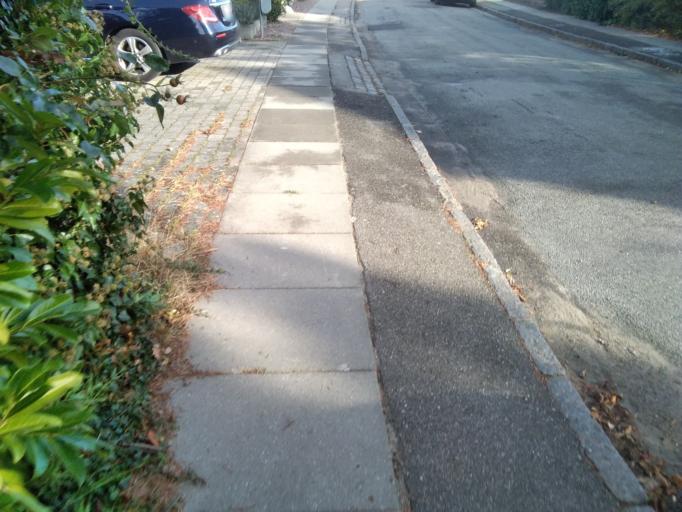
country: DK
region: Capital Region
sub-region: Kobenhavn
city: Vanlose
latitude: 55.6997
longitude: 12.4943
